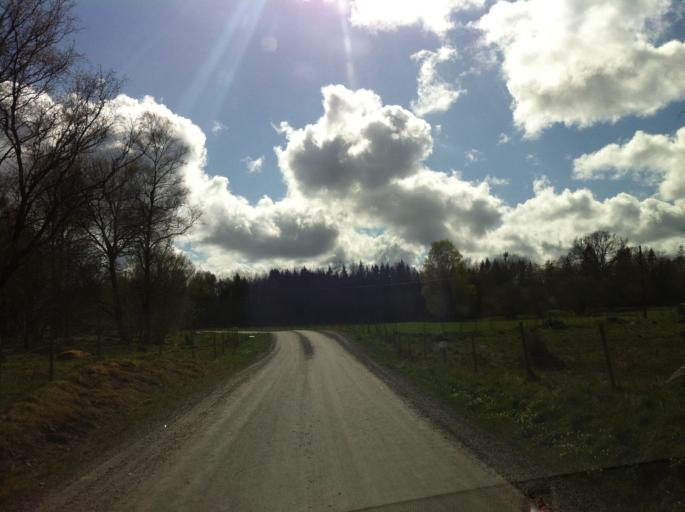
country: SE
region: Vaestra Goetaland
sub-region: Bollebygds Kommun
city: Bollebygd
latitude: 57.7696
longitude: 12.5913
